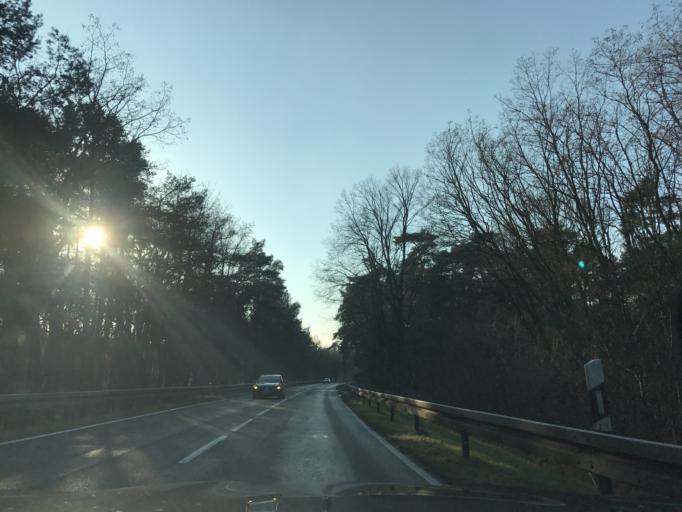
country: DE
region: Brandenburg
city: Wenzlow
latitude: 52.2814
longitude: 12.4421
